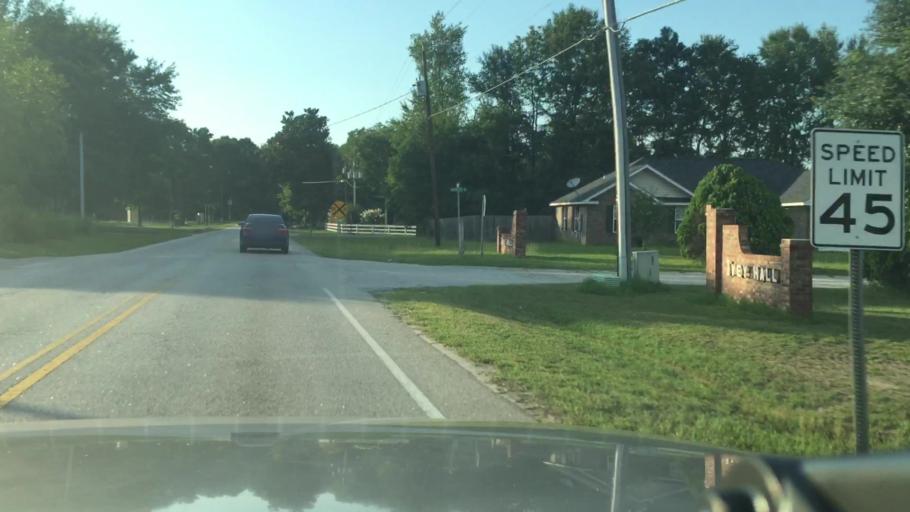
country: US
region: South Carolina
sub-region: Sumter County
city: South Sumter
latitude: 33.8930
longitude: -80.3678
